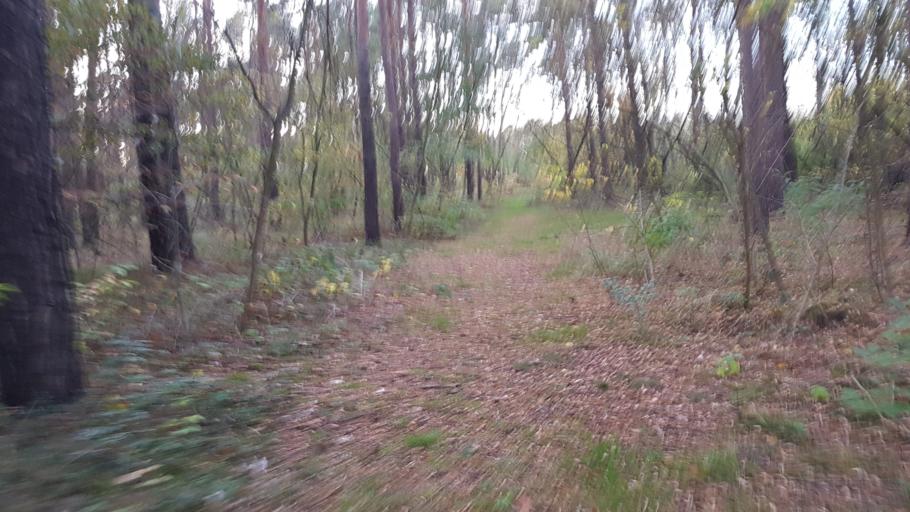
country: DE
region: Brandenburg
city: Bad Liebenwerda
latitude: 51.5448
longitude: 13.4297
